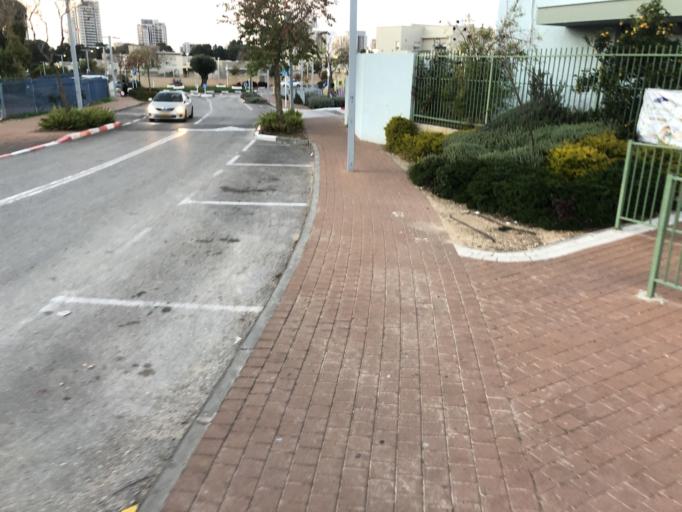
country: IL
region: Northern District
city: `Akko
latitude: 32.9337
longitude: 35.0905
